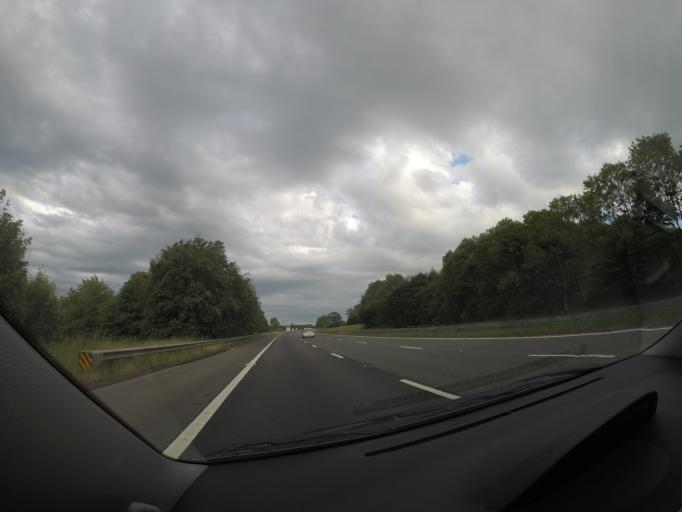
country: GB
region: England
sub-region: Cumbria
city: Penrith
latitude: 54.7563
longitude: -2.8219
